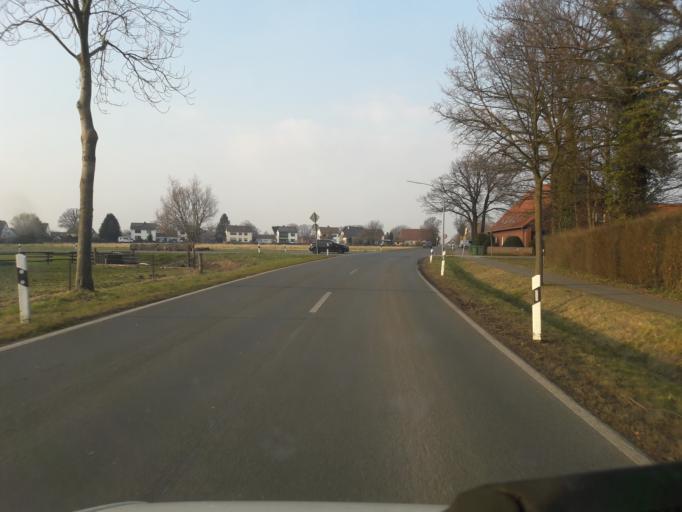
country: DE
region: North Rhine-Westphalia
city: Espelkamp
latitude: 52.3446
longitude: 8.6505
